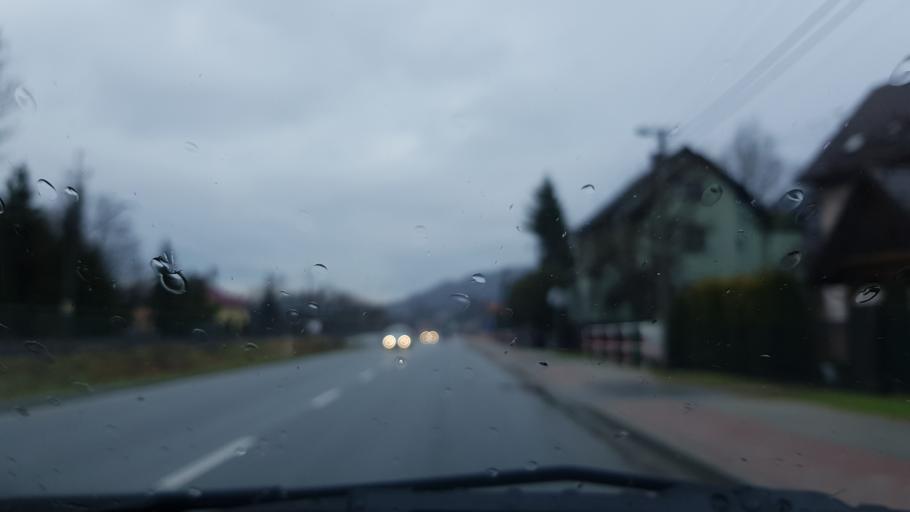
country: PL
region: Lesser Poland Voivodeship
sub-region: Powiat suski
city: Sucha Beskidzka
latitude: 49.7360
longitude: 19.5573
